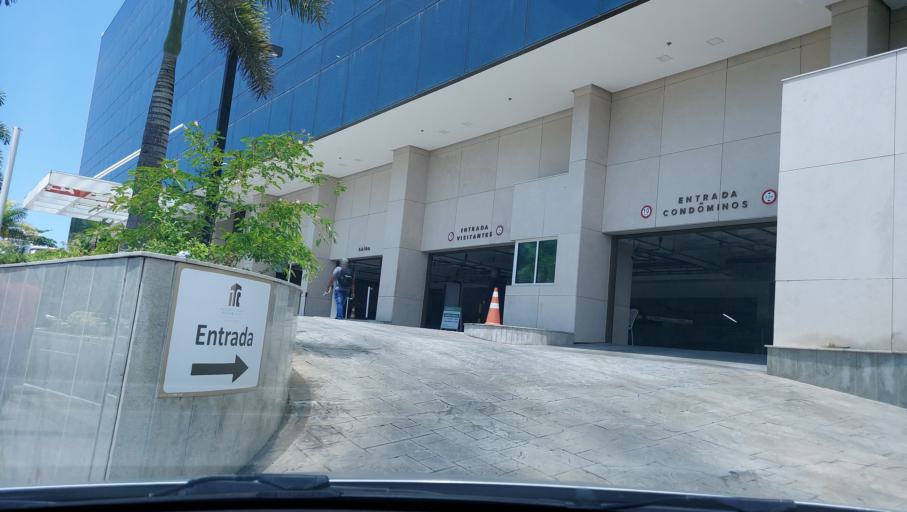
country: BR
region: Bahia
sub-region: Salvador
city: Salvador
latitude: -12.9868
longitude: -38.4486
